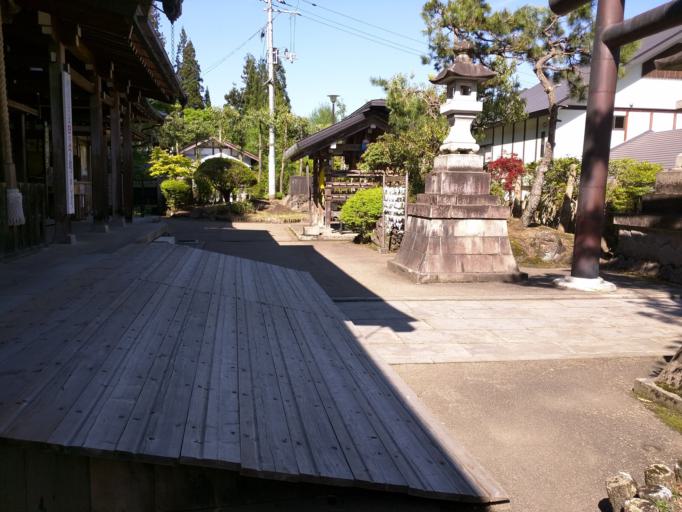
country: JP
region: Fukushima
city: Kitakata
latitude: 37.5563
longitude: 139.6229
